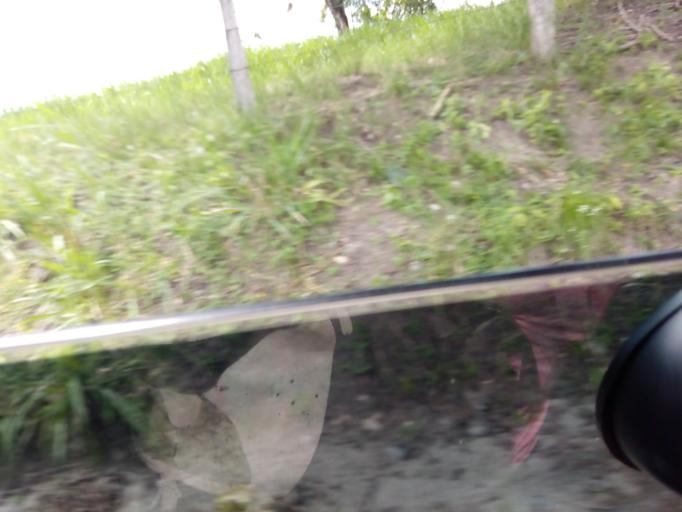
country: CO
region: Boyaca
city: Puerto Boyaca
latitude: 5.9729
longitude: -74.4315
